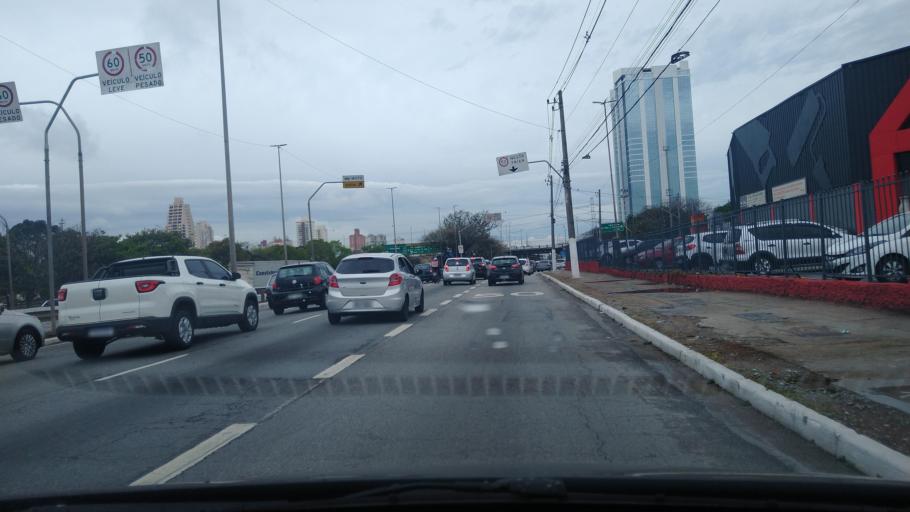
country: SA
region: Ar Riyad
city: Ad Dilam
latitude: 23.5158
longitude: 46.6694
